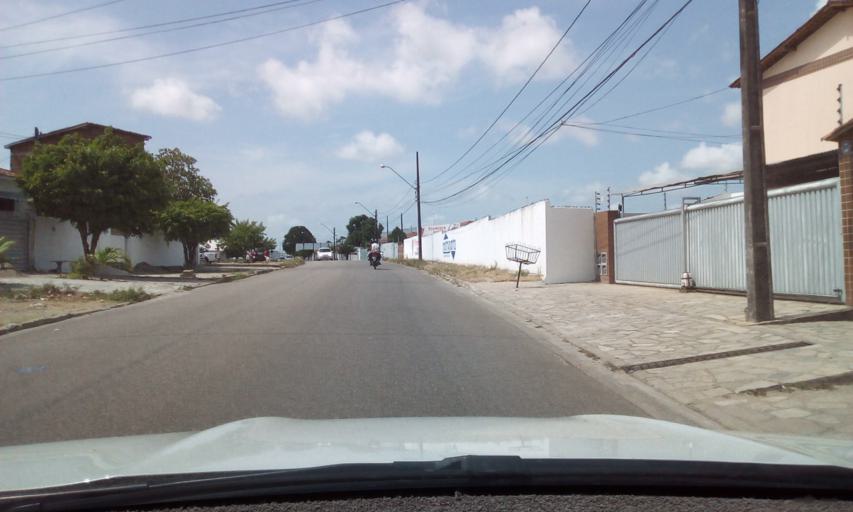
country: BR
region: Paraiba
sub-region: Joao Pessoa
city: Joao Pessoa
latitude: -7.1748
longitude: -34.8652
